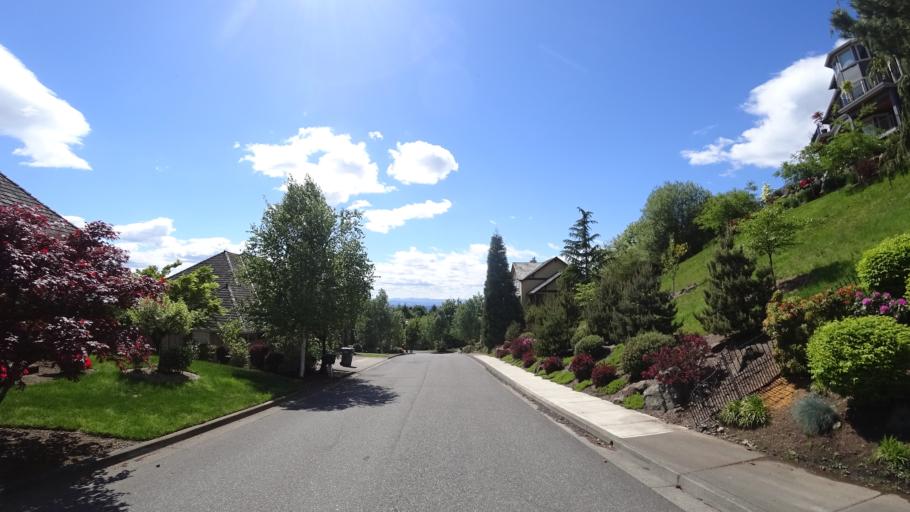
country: US
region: Oregon
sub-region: Washington County
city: West Haven
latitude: 45.5490
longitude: -122.7794
